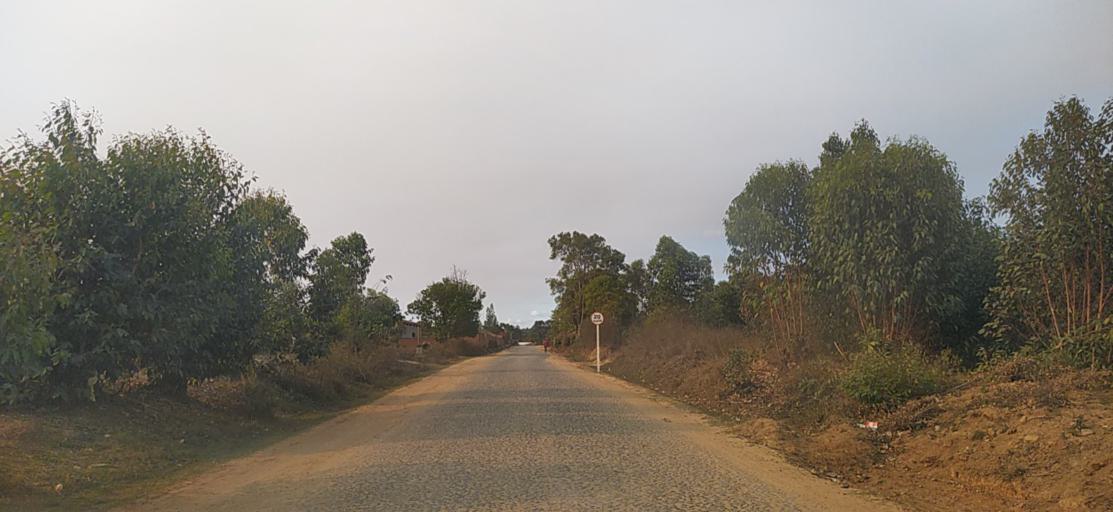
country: MG
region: Alaotra Mangoro
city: Moramanga
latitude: -18.6157
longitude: 48.2772
